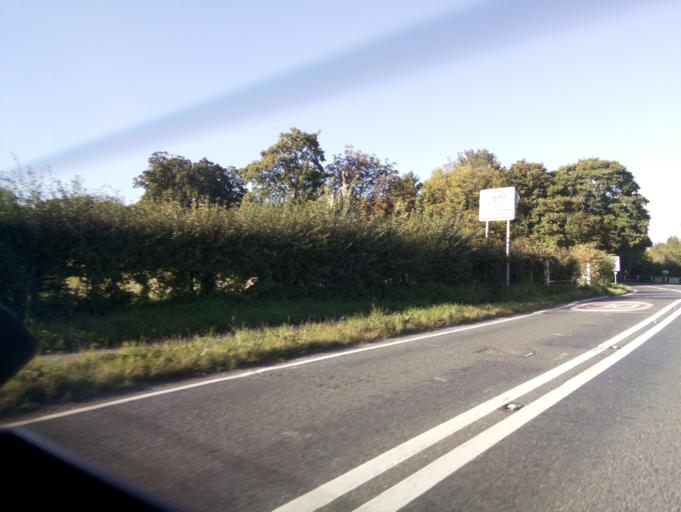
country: GB
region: England
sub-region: Hampshire
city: Swanmore
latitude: 50.9767
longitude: -1.1315
